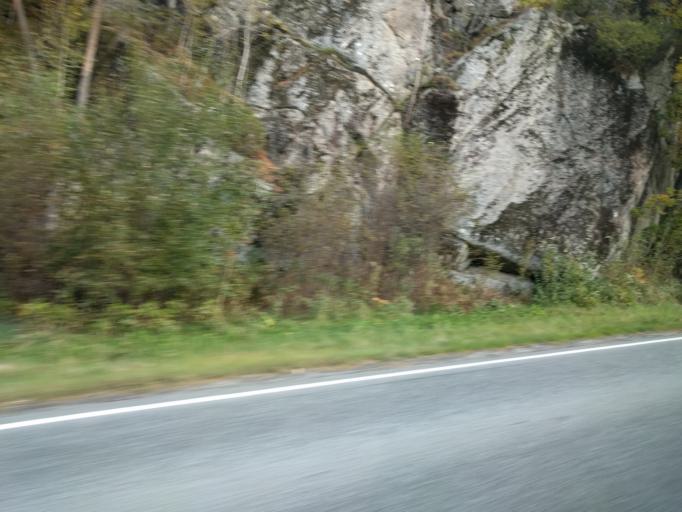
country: NO
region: Vest-Agder
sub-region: Songdalen
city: Nodeland
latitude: 58.2539
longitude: 7.8425
